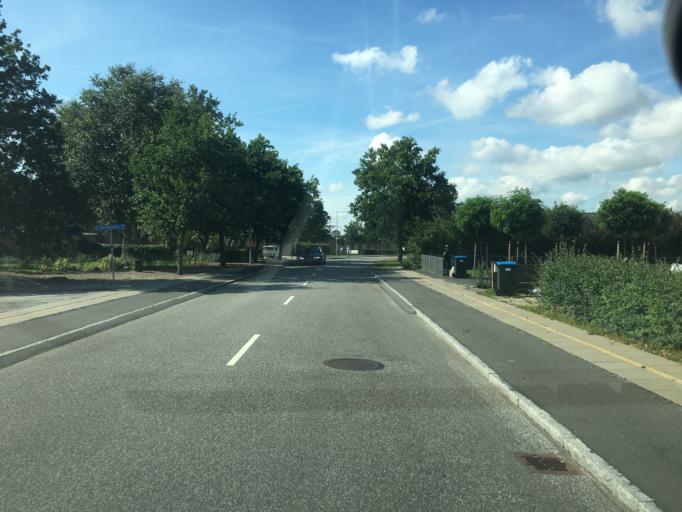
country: DK
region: South Denmark
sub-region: Tonder Kommune
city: Tonder
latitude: 54.9362
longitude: 8.8519
